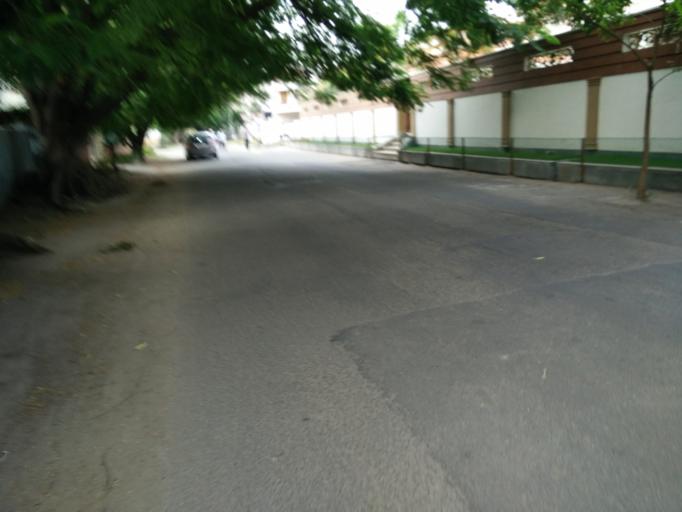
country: IN
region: Tamil Nadu
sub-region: Coimbatore
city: Coimbatore
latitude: 11.0216
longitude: 76.9444
